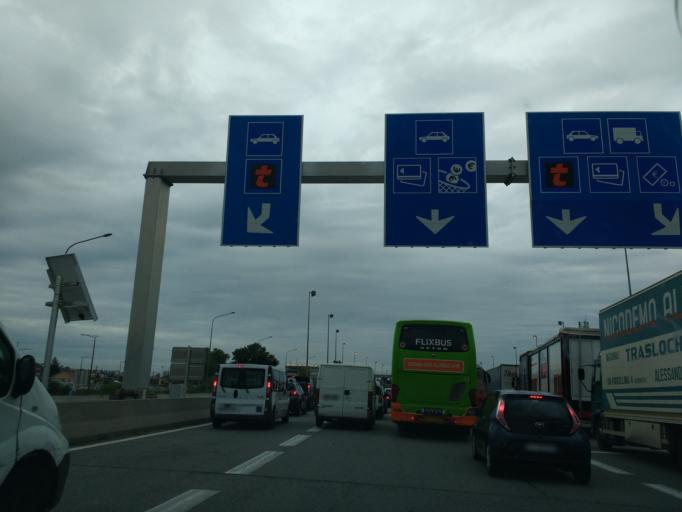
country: FR
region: Provence-Alpes-Cote d'Azur
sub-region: Departement des Alpes-Maritimes
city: Saint-Laurent-du-Var
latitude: 43.7019
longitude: 7.1882
